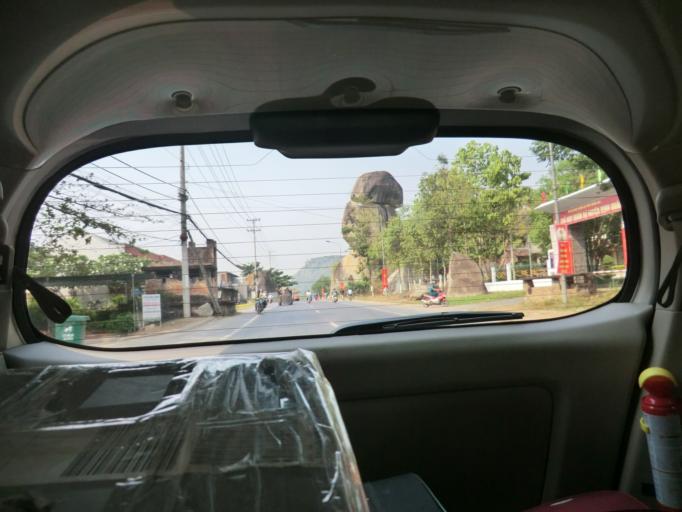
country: VN
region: Dong Nai
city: Tan Phu
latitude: 11.1915
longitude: 107.3489
